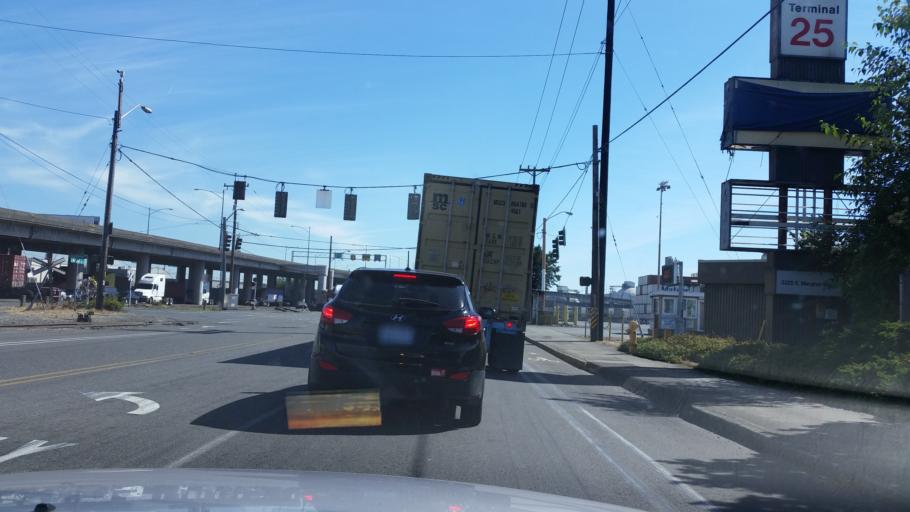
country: US
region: Washington
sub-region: King County
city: Seattle
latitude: 47.5761
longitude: -122.3401
